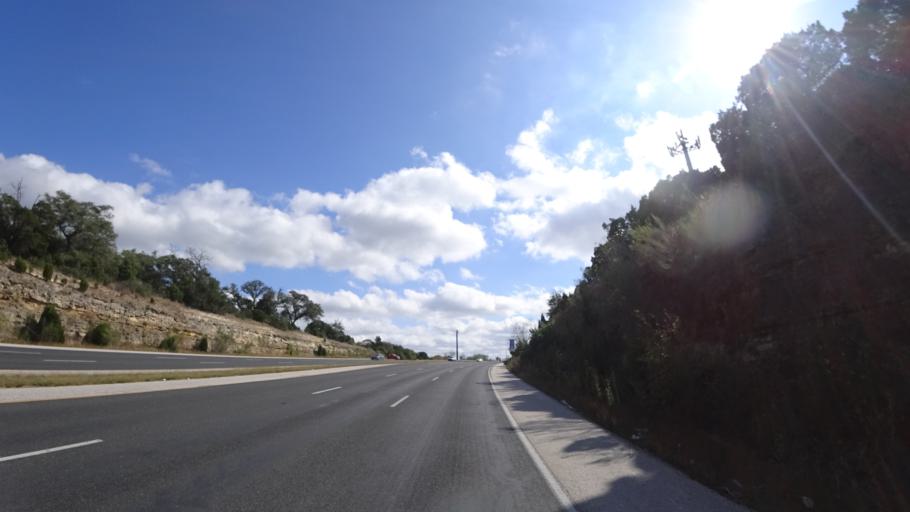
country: US
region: Texas
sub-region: Travis County
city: Barton Creek
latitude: 30.2612
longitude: -97.8857
